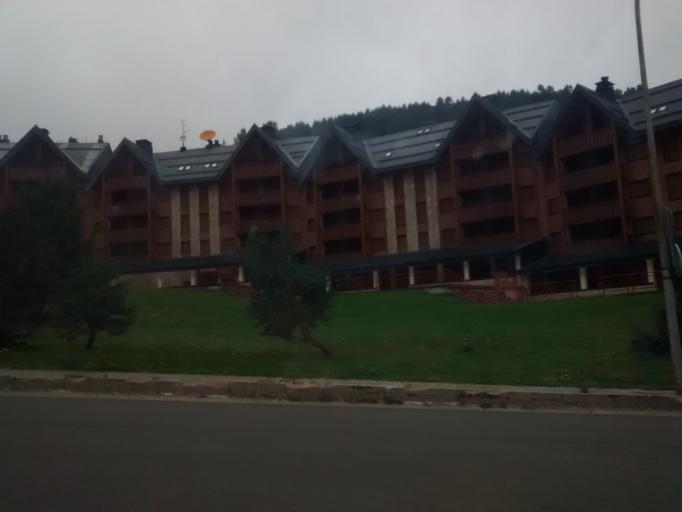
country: ES
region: Aragon
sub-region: Provincia de Huesca
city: Canfranc
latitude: 42.7868
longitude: -0.5287
